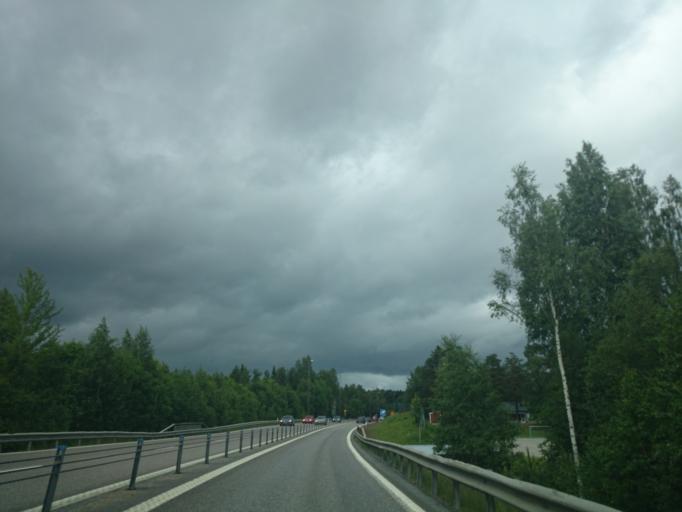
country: SE
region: Vaesternorrland
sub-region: Sundsvalls Kommun
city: Njurundabommen
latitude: 62.2669
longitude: 17.3702
